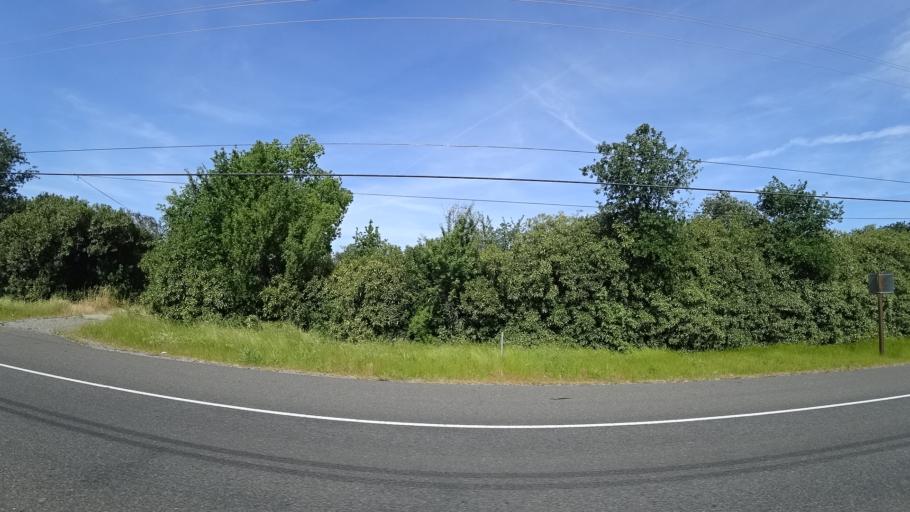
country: US
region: California
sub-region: Tehama County
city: Gerber
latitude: 40.1386
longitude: -122.1294
